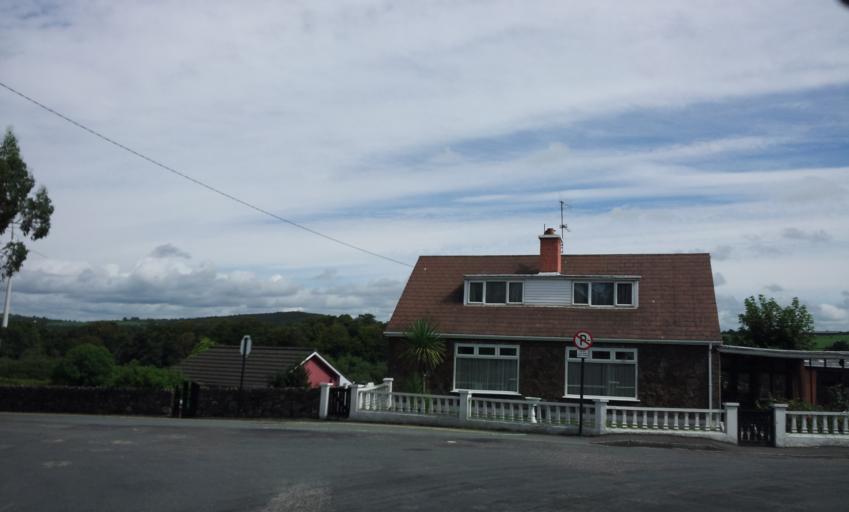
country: IE
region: Munster
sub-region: Ciarrai
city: Killorglin
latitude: 52.1083
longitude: -9.7859
